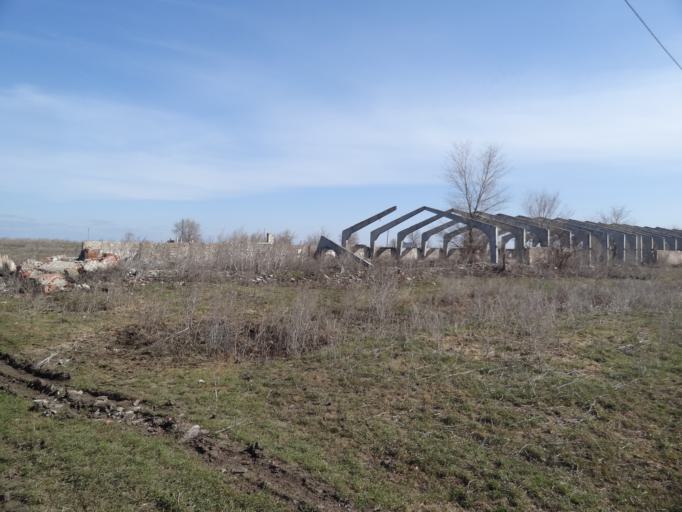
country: RU
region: Saratov
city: Engel's
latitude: 51.4261
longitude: 46.1894
